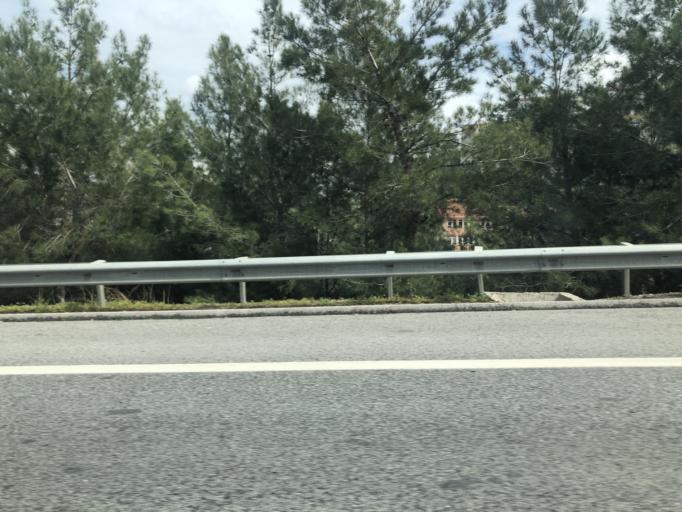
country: TR
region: Izmir
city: Karabaglar
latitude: 38.3907
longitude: 27.0636
